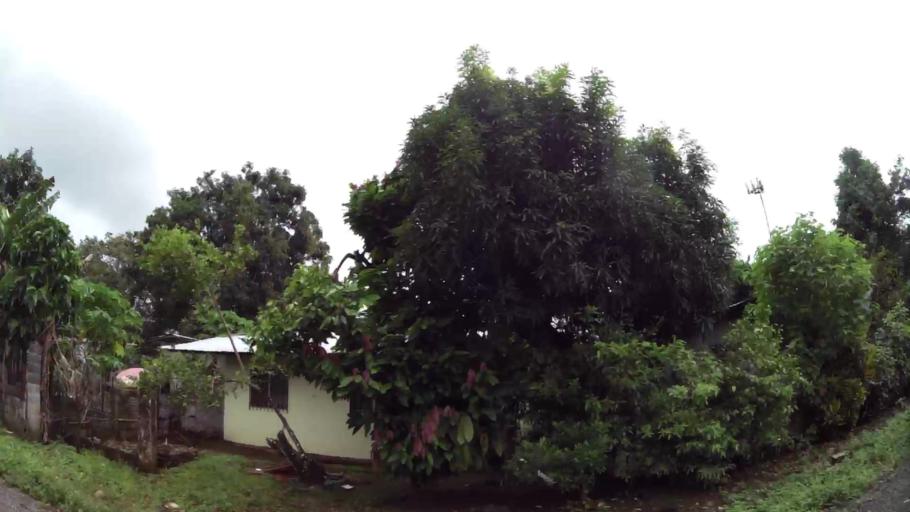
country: PA
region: Chiriqui
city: David
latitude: 8.4157
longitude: -82.4497
